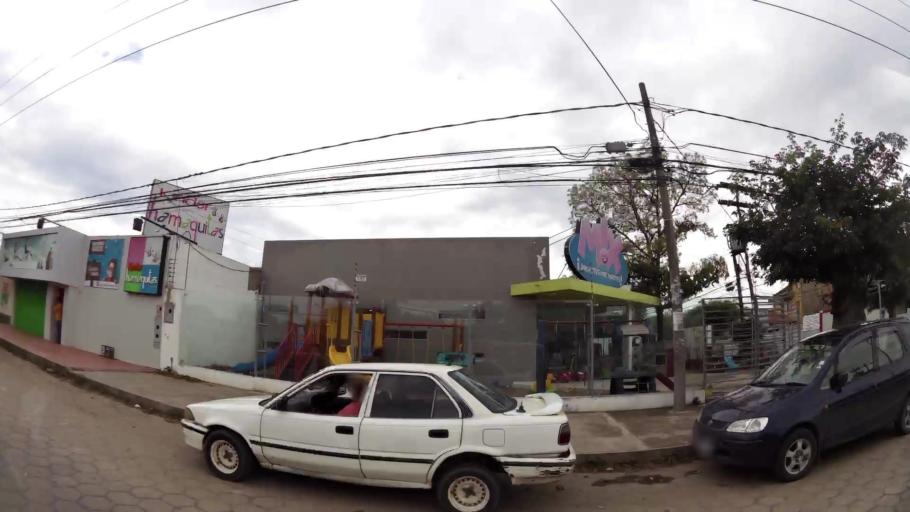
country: BO
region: Santa Cruz
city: Santa Cruz de la Sierra
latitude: -17.7533
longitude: -63.1709
